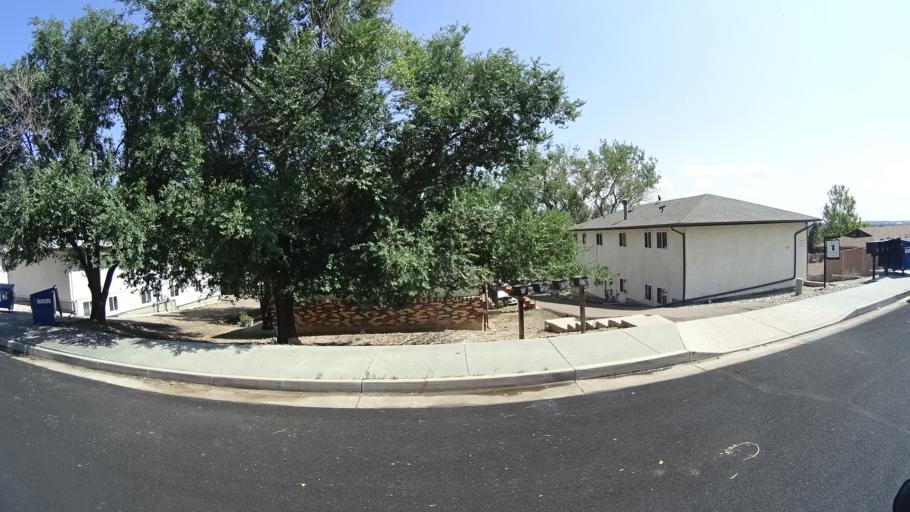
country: US
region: Colorado
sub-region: El Paso County
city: Colorado Springs
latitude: 38.8748
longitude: -104.8396
